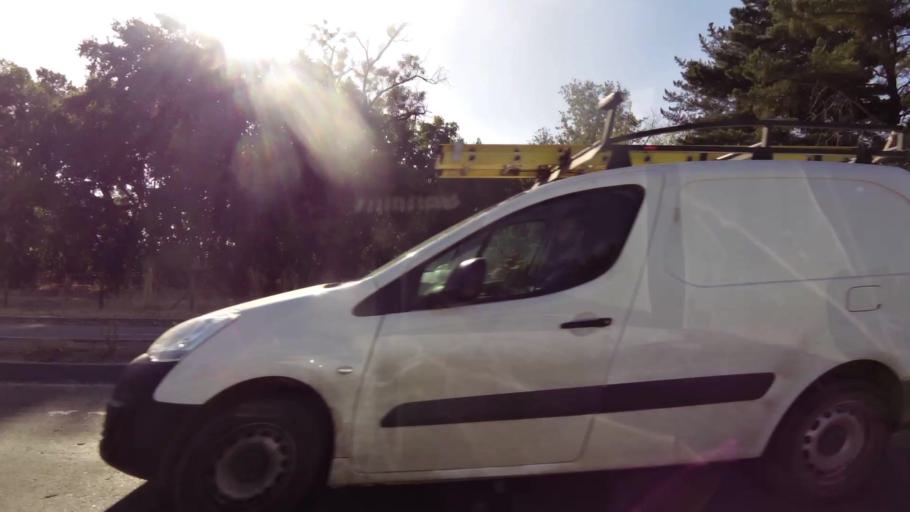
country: CL
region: Maule
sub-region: Provincia de Talca
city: Talca
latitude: -35.4182
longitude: -71.6744
